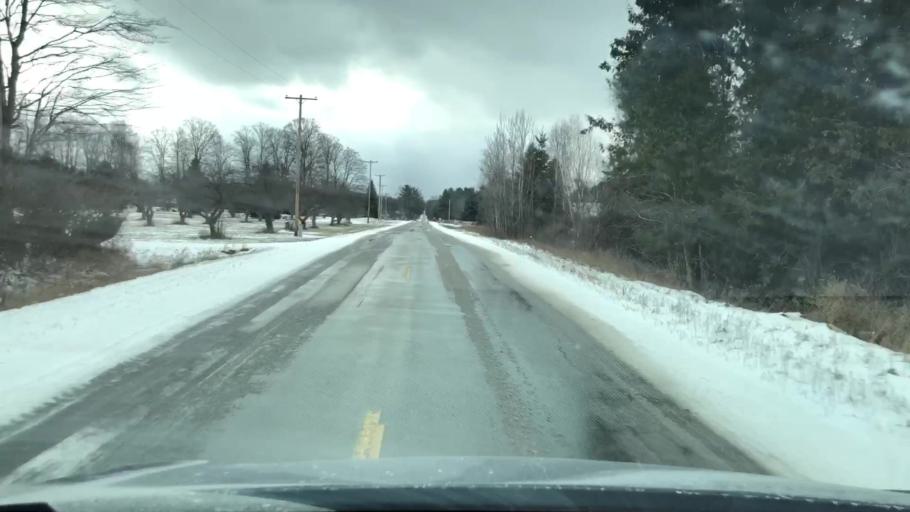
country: US
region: Michigan
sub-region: Antrim County
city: Elk Rapids
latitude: 44.9127
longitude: -85.5154
